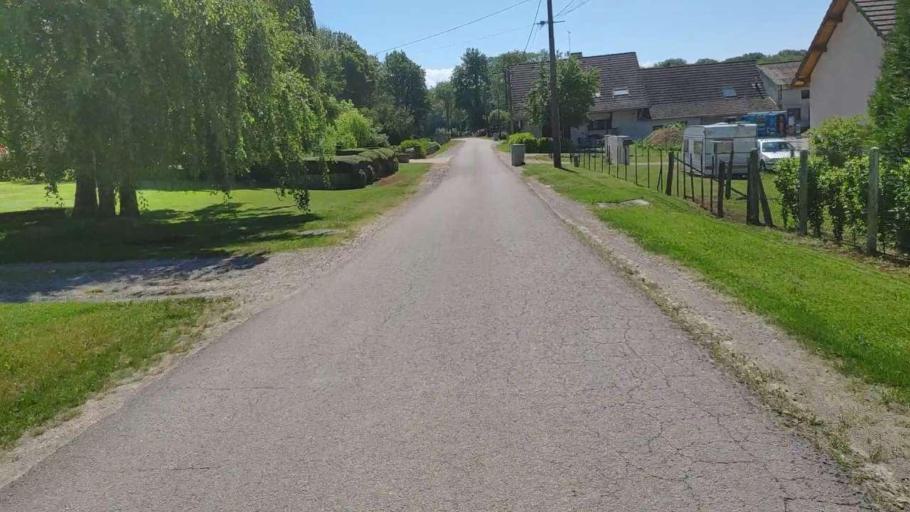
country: FR
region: Franche-Comte
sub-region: Departement du Jura
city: Bletterans
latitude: 46.7650
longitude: 5.4362
